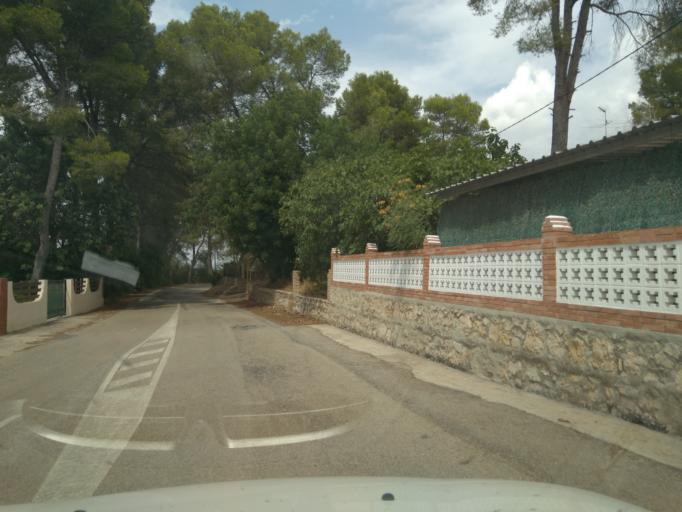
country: ES
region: Valencia
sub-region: Provincia de Valencia
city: Rafelguaraf
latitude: 39.0802
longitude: -0.4235
